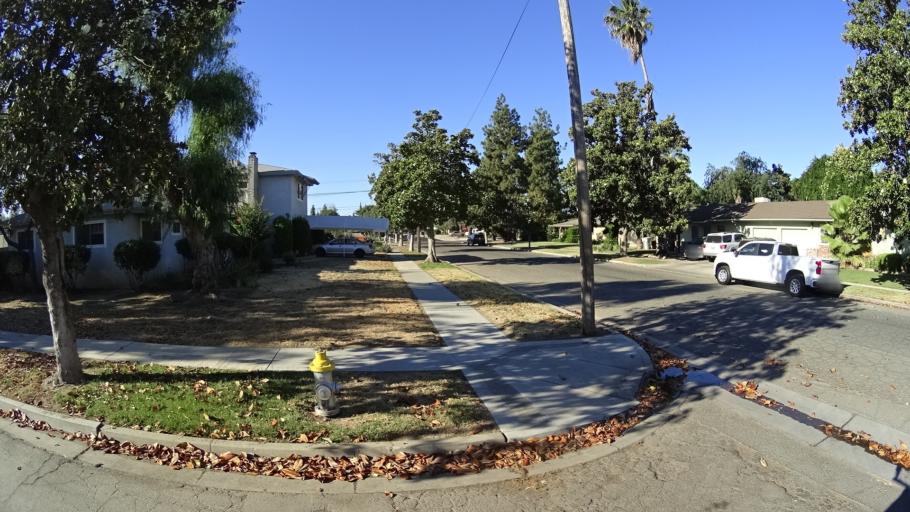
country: US
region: California
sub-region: Fresno County
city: Fresno
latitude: 36.8019
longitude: -119.8196
